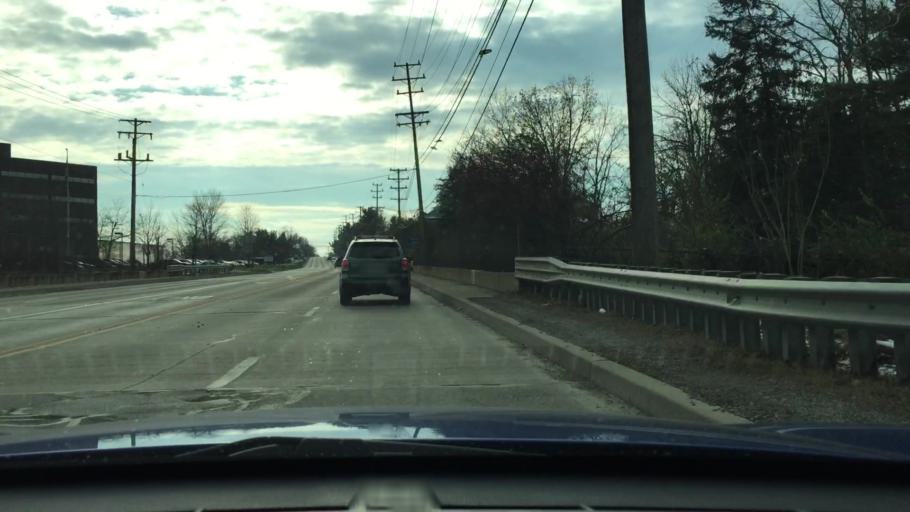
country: US
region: Pennsylvania
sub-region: Allegheny County
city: Heidelberg
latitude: 40.3806
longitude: -80.0953
